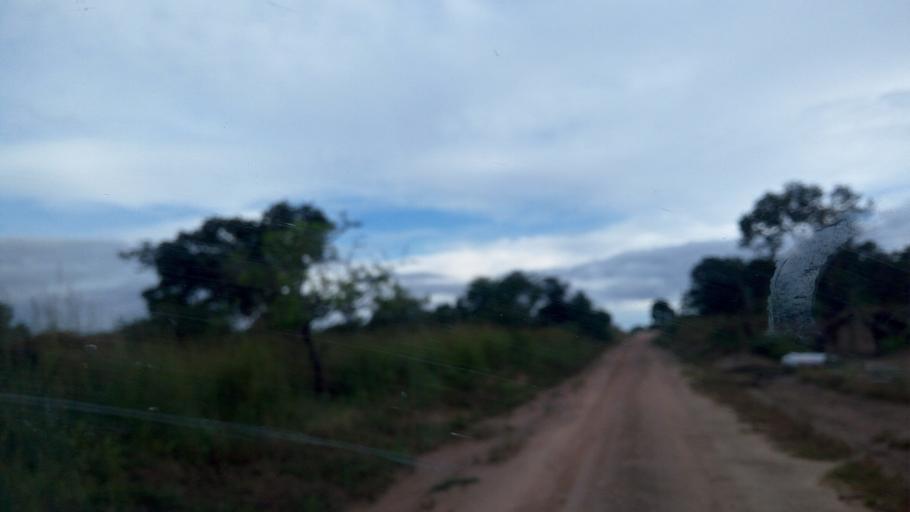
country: CD
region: Katanga
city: Kalemie
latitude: -6.5888
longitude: 29.0380
